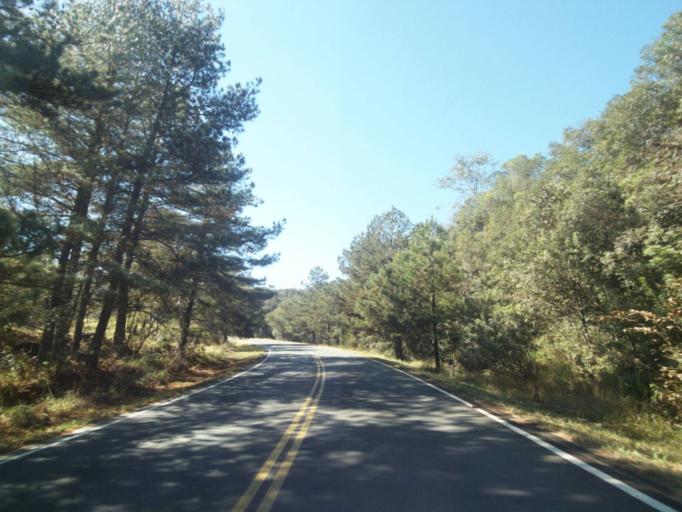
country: BR
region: Parana
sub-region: Telemaco Borba
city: Telemaco Borba
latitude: -24.4244
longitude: -50.5820
